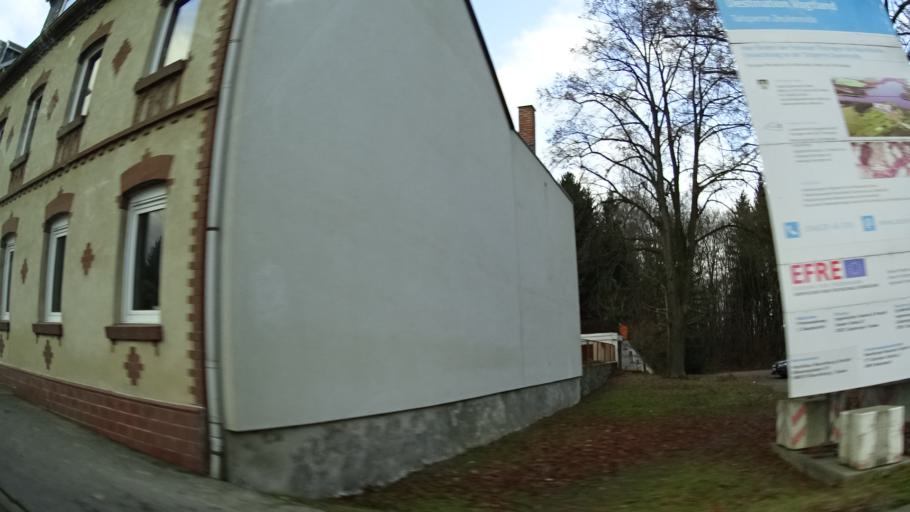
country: DE
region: Thuringia
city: Zeulenroda
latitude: 50.6616
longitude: 11.9759
